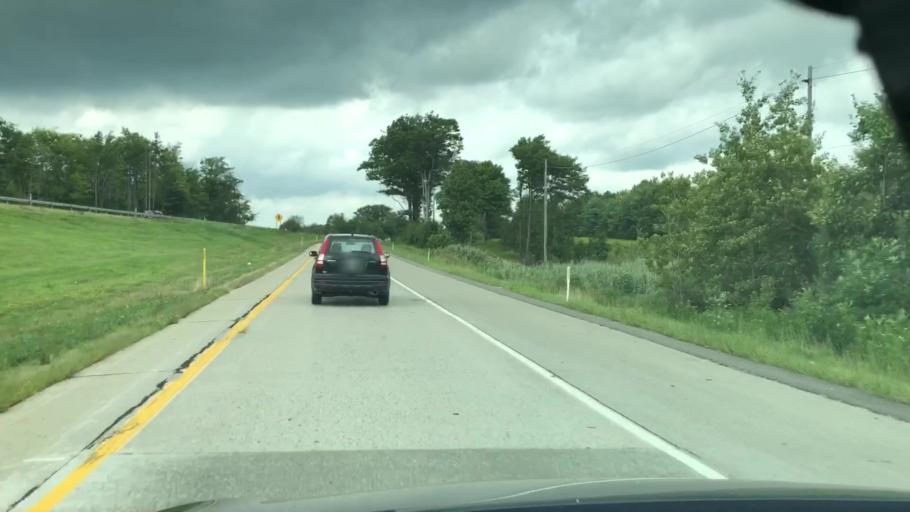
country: US
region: Pennsylvania
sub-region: Erie County
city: Edinboro
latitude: 41.8816
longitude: -80.1751
